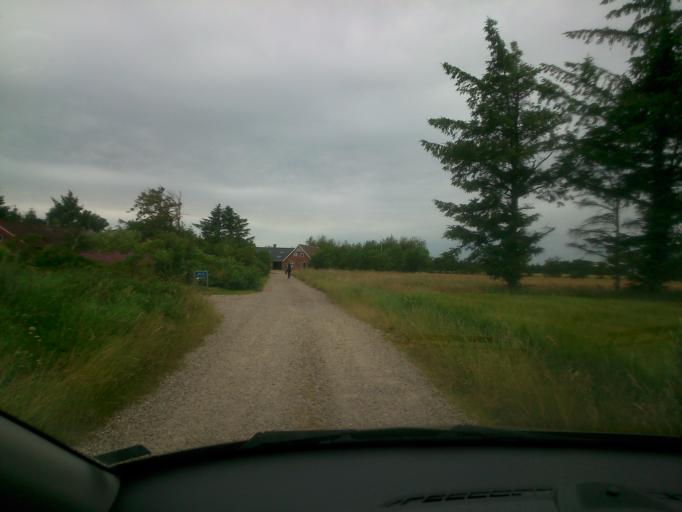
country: DK
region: Central Jutland
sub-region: Ringkobing-Skjern Kommune
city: Skjern
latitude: 55.9583
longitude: 8.3720
